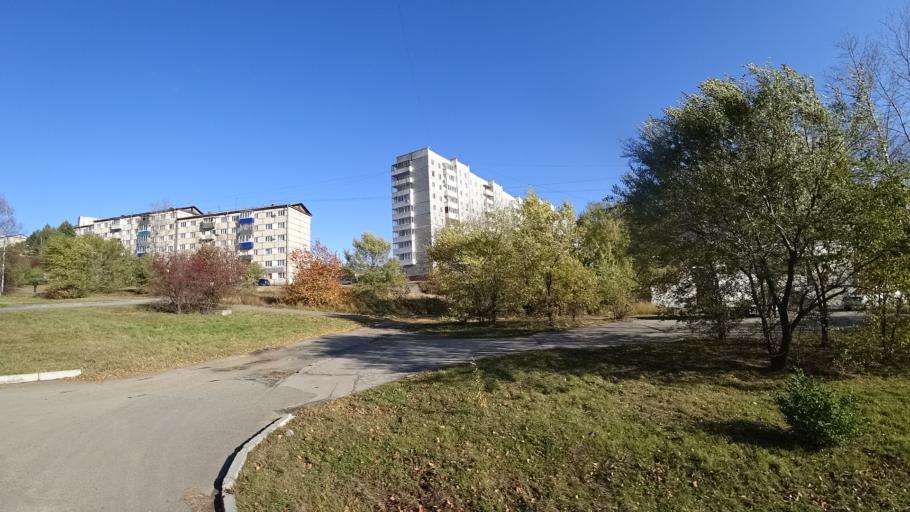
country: RU
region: Khabarovsk Krai
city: Amursk
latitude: 50.2392
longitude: 136.9116
